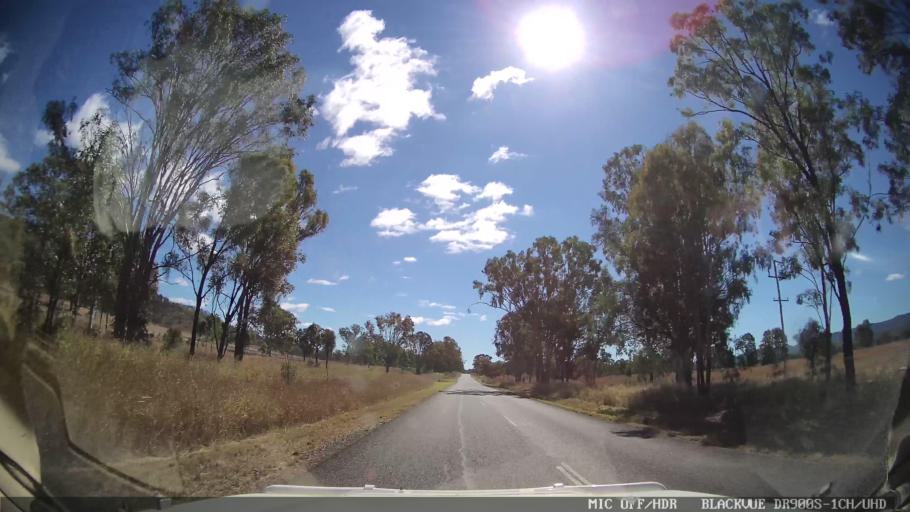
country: AU
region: Queensland
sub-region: Gladstone
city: Toolooa
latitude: -24.4479
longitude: 151.3439
